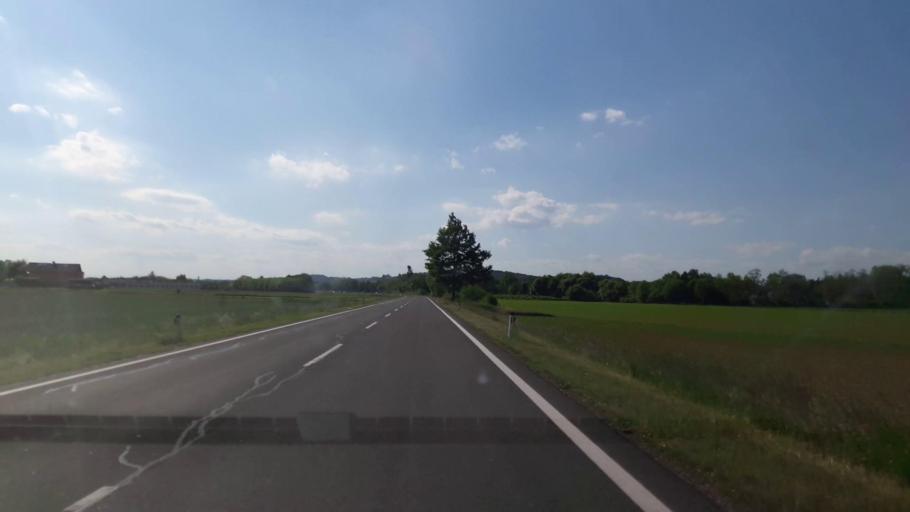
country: AT
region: Styria
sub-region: Politischer Bezirk Suedoststeiermark
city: Fehring
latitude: 46.9392
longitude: 16.0337
